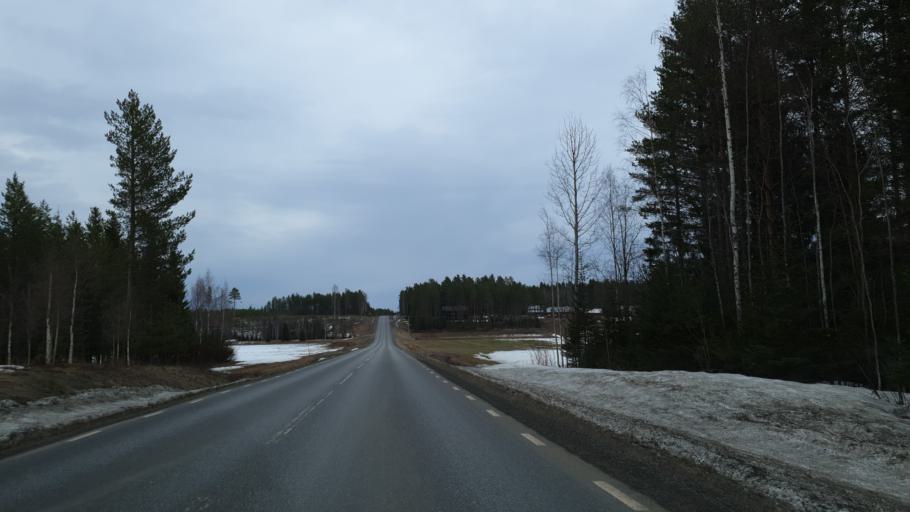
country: SE
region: Vaesterbotten
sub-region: Robertsfors Kommun
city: Robertsfors
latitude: 64.2178
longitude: 20.9014
